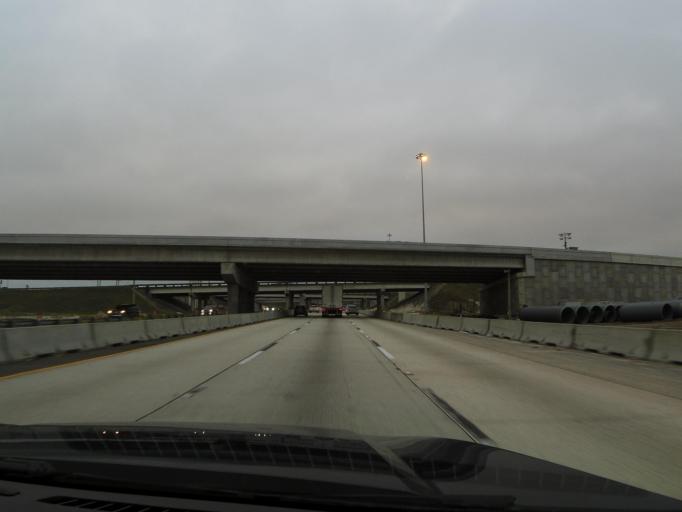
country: US
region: Florida
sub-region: Duval County
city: Jacksonville
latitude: 30.4613
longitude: -81.6494
